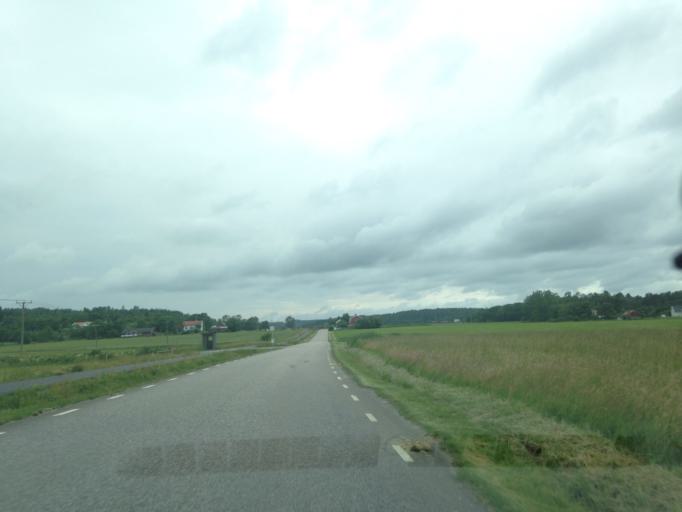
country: SE
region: Vaestra Goetaland
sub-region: Goteborg
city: Torslanda
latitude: 57.8208
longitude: 11.8276
